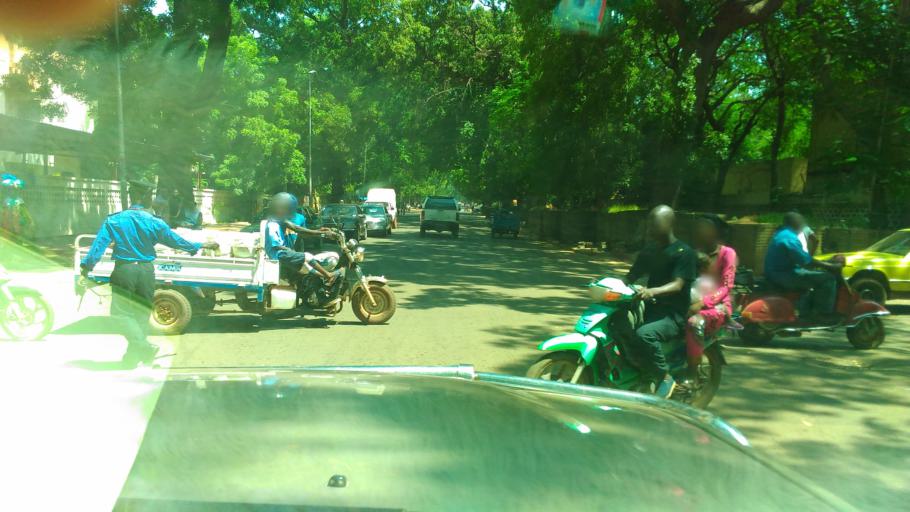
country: ML
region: Bamako
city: Bamako
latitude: 12.6513
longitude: -7.9999
